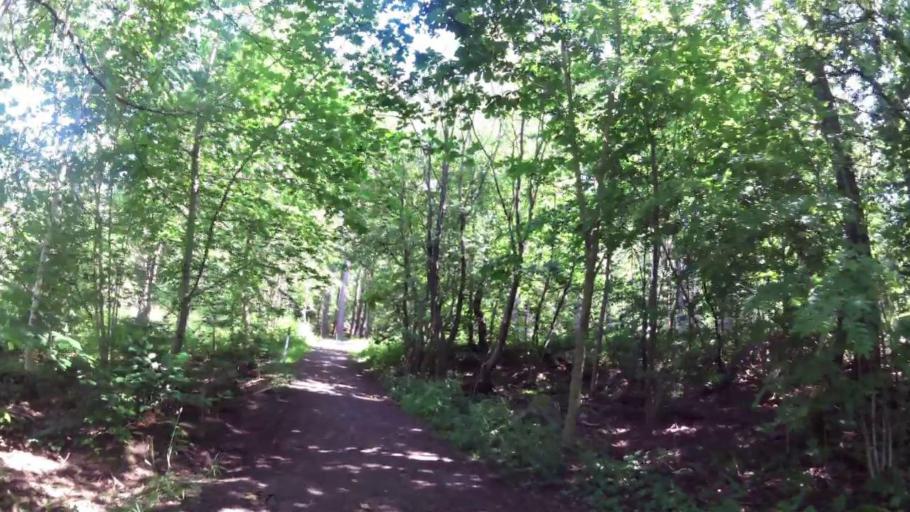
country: SE
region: OEstergoetland
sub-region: Linkopings Kommun
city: Linkoping
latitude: 58.4001
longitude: 15.6002
